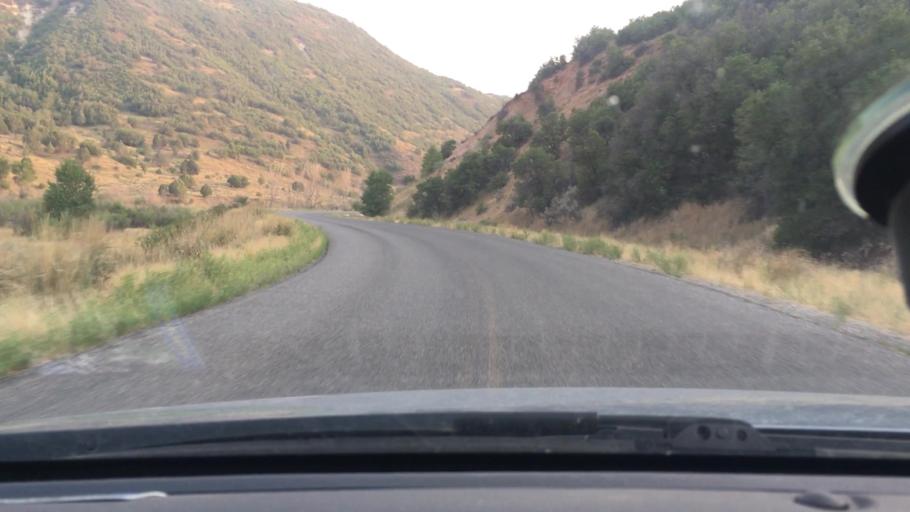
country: US
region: Utah
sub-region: Utah County
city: Mapleton
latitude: 40.0511
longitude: -111.4649
